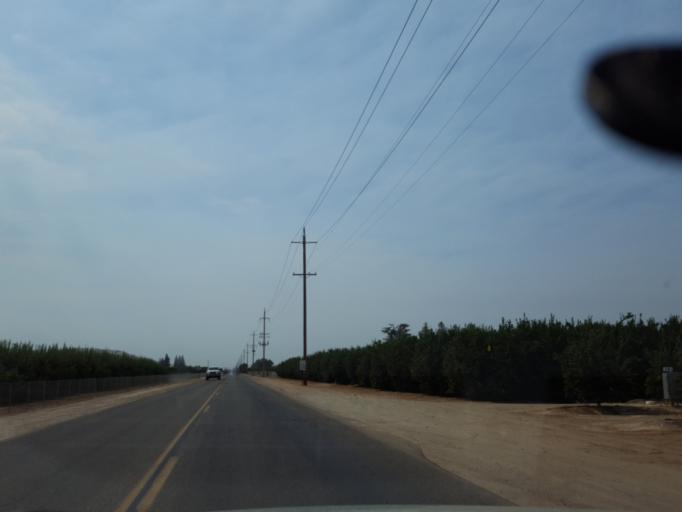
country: US
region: California
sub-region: Fresno County
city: Orange Cove
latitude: 36.6027
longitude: -119.3048
